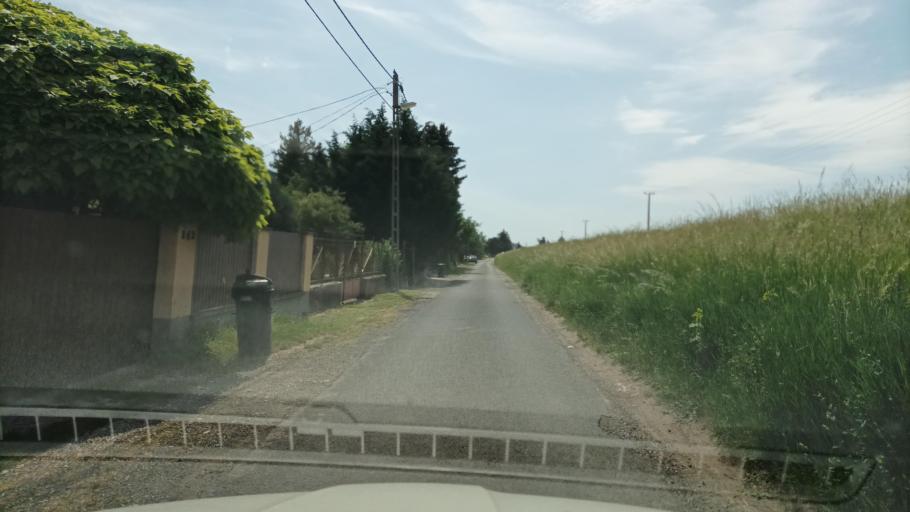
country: HU
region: Pest
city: Rackeve
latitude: 47.1372
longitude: 18.9585
